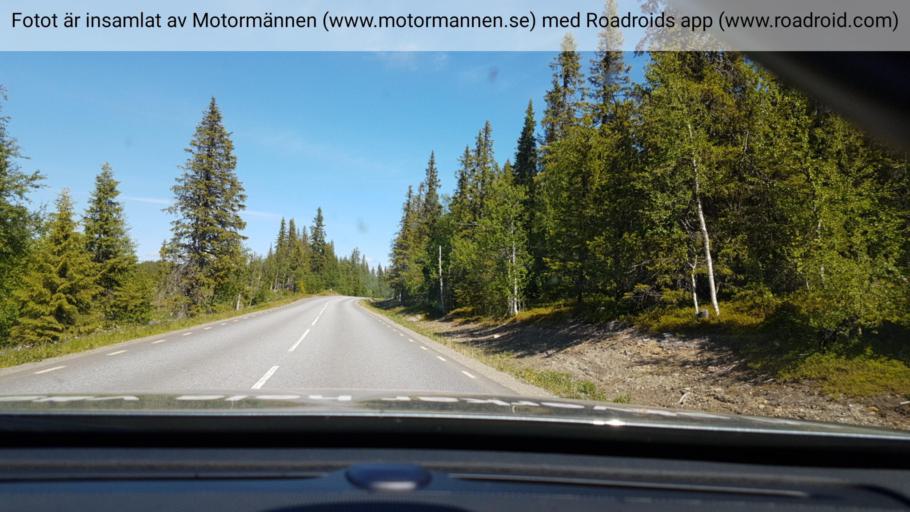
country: SE
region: Vaesterbotten
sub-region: Asele Kommun
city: Insjon
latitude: 64.7240
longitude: 17.3473
